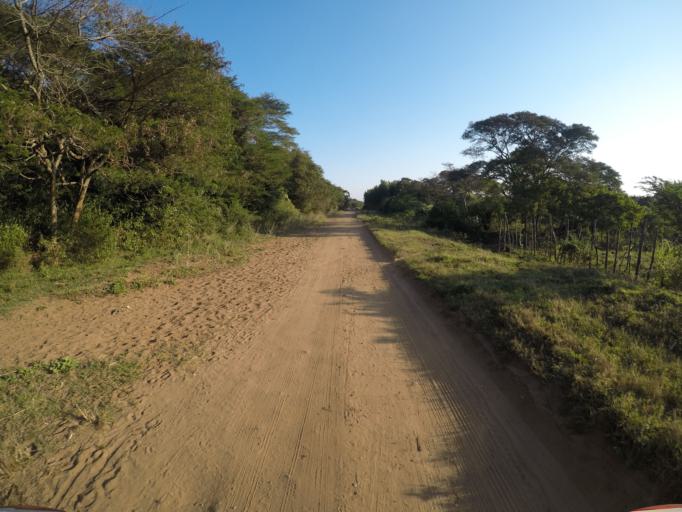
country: ZA
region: KwaZulu-Natal
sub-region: uThungulu District Municipality
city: KwaMbonambi
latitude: -28.7011
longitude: 32.1915
